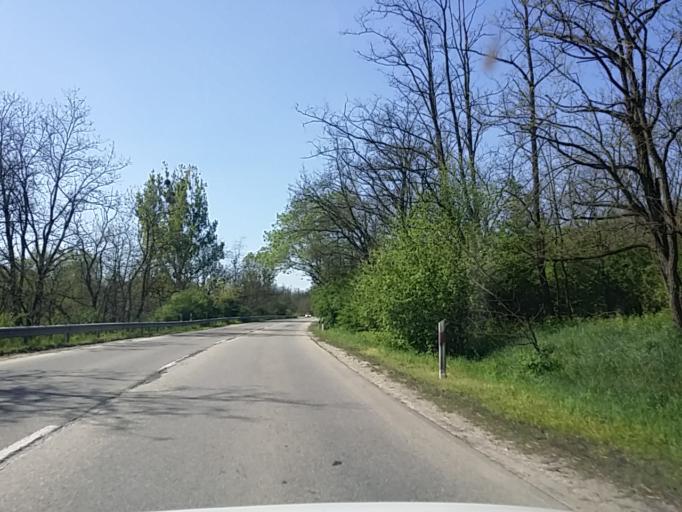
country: HU
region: Pest
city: Godollo
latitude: 47.6066
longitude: 19.4068
